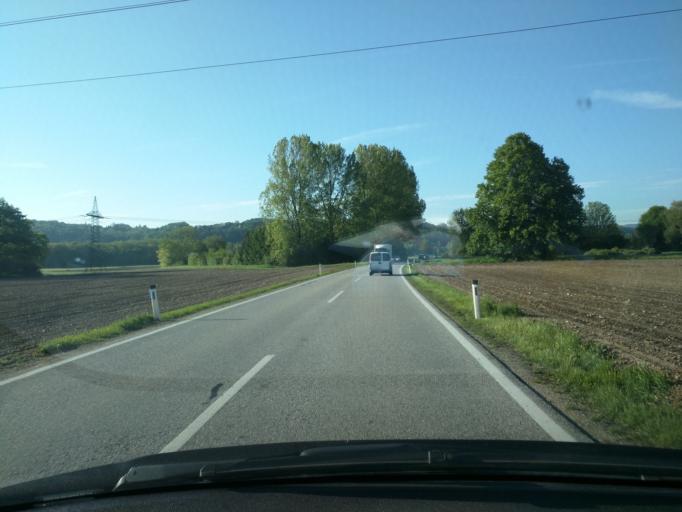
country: AT
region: Lower Austria
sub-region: Politischer Bezirk Melk
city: Blindenmarkt
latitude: 48.1245
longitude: 15.0131
